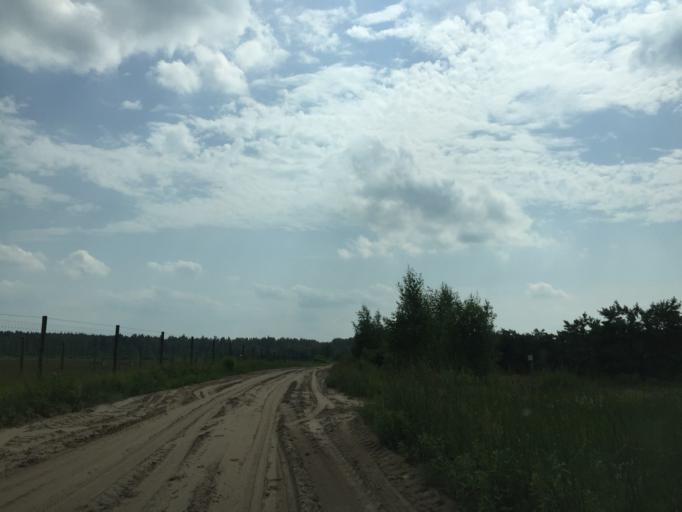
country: LV
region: Ozolnieku
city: Ozolnieki
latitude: 56.7616
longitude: 23.7533
